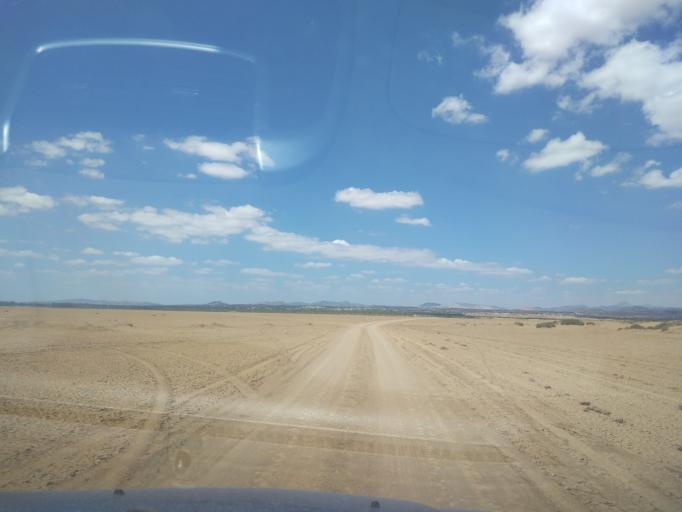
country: TN
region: Susah
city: Harqalah
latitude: 36.1613
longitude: 10.4599
